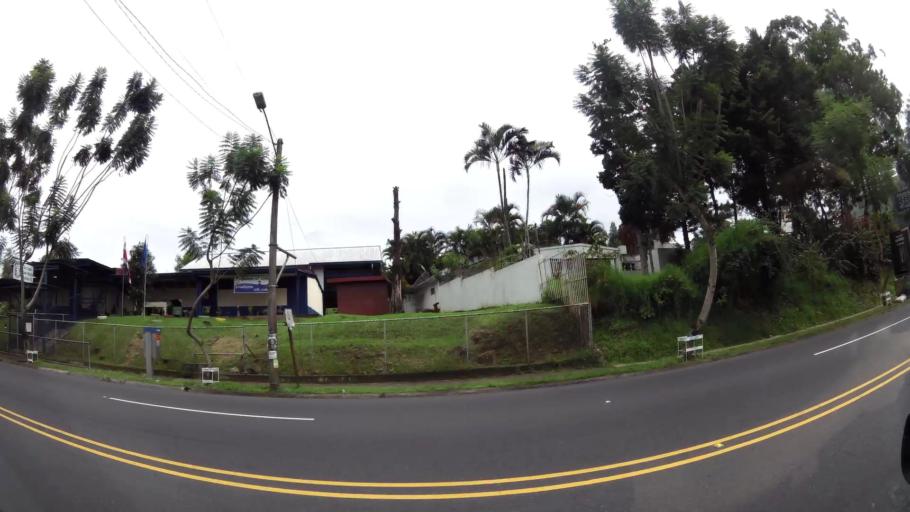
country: CR
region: San Jose
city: Curridabat
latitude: 9.9168
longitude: -84.0415
